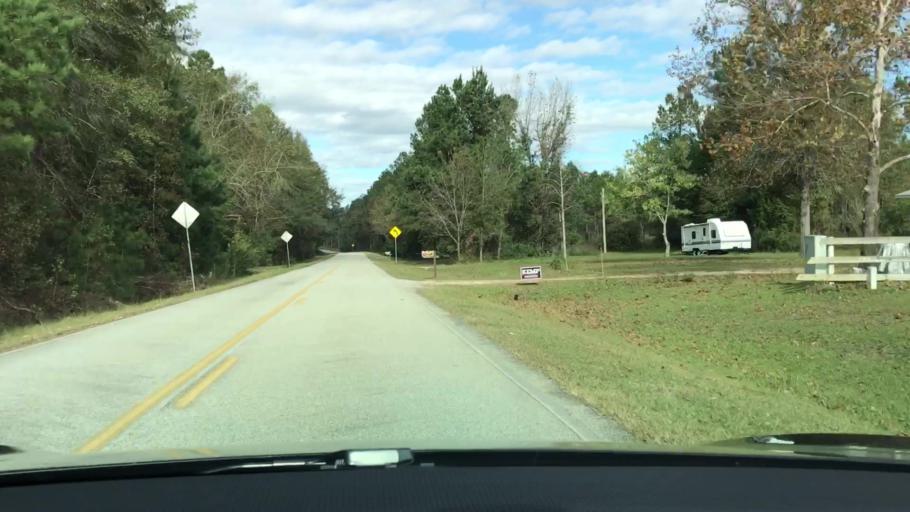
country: US
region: Georgia
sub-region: Jefferson County
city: Wadley
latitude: 32.8027
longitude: -82.3866
